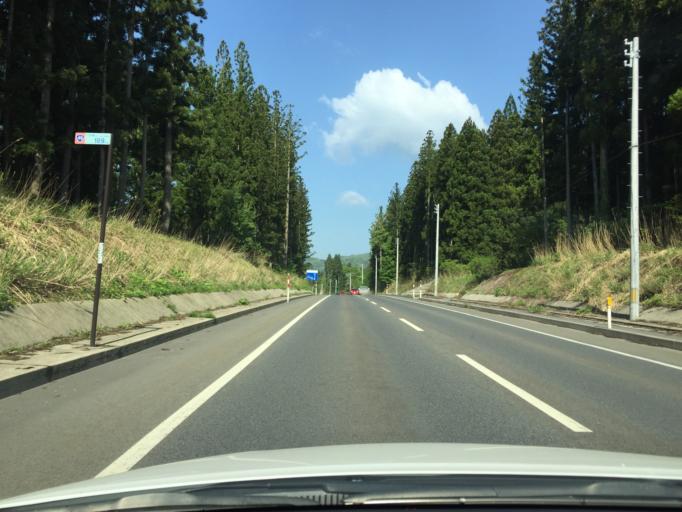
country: JP
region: Niigata
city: Suibara
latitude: 37.6805
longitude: 139.4449
